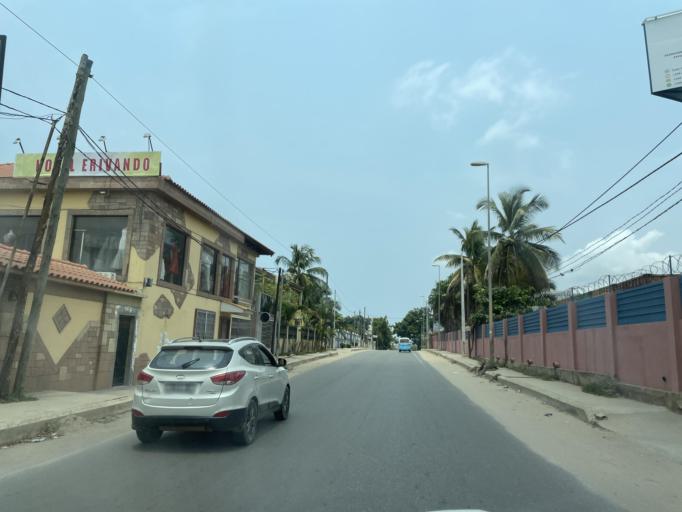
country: AO
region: Luanda
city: Luanda
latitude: -8.9382
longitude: 13.1696
